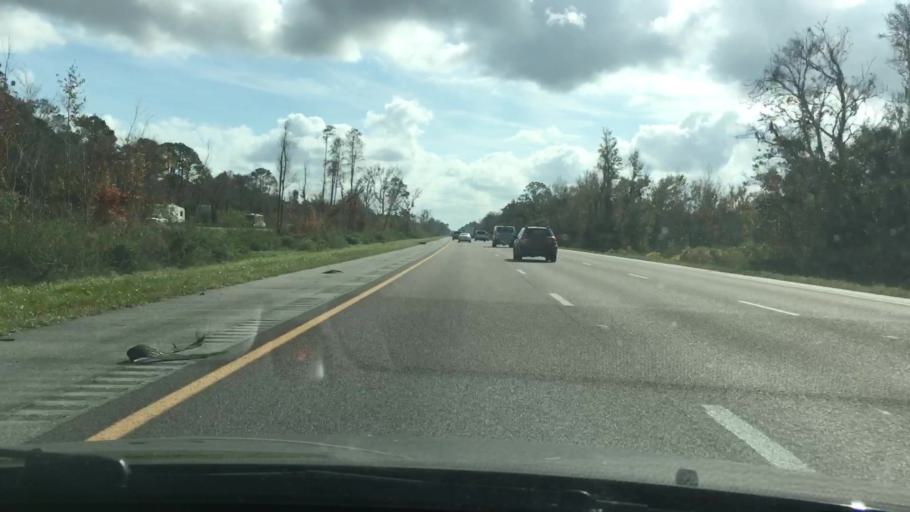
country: US
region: Florida
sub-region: Volusia County
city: Oak Hill
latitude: 28.9016
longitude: -80.9318
